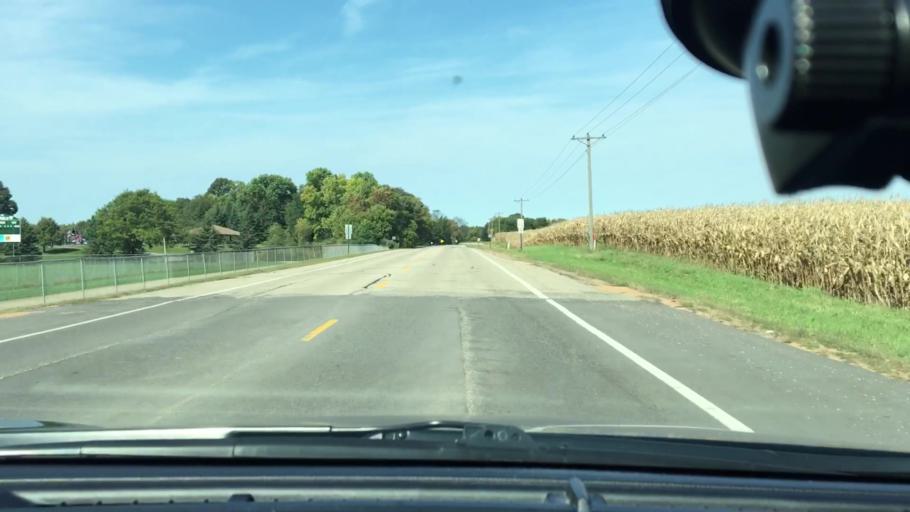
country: US
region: Minnesota
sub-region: Hennepin County
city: Corcoran
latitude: 45.0963
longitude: -93.5497
